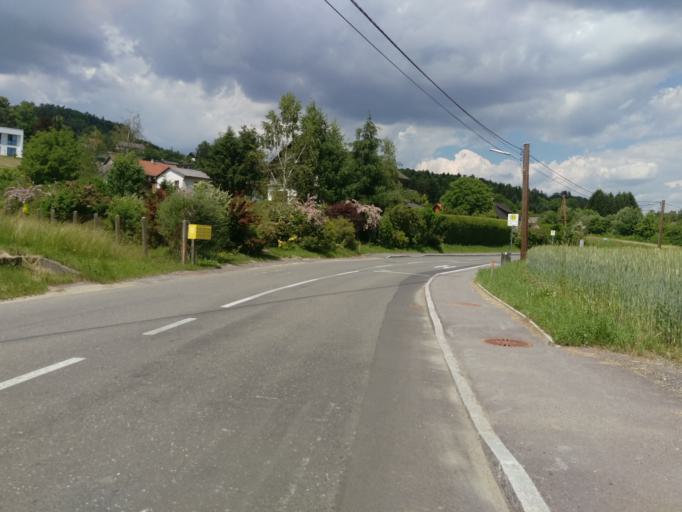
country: AT
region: Styria
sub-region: Graz Stadt
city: Mariatrost
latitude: 47.0973
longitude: 15.5046
